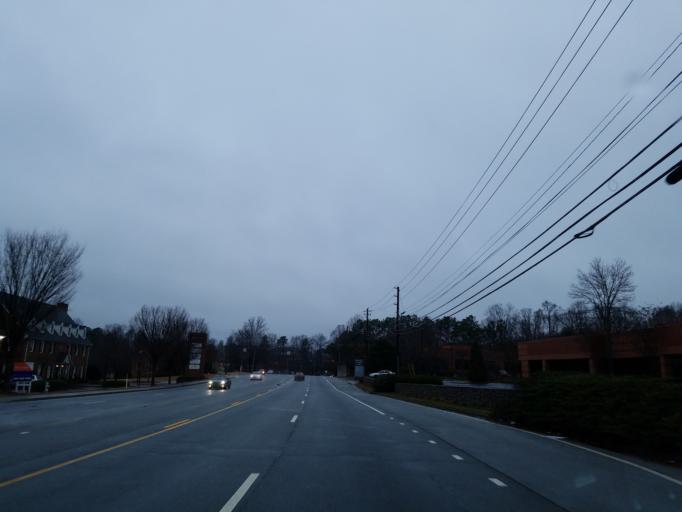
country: US
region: Georgia
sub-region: Gwinnett County
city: Norcross
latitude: 33.9633
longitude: -84.2508
